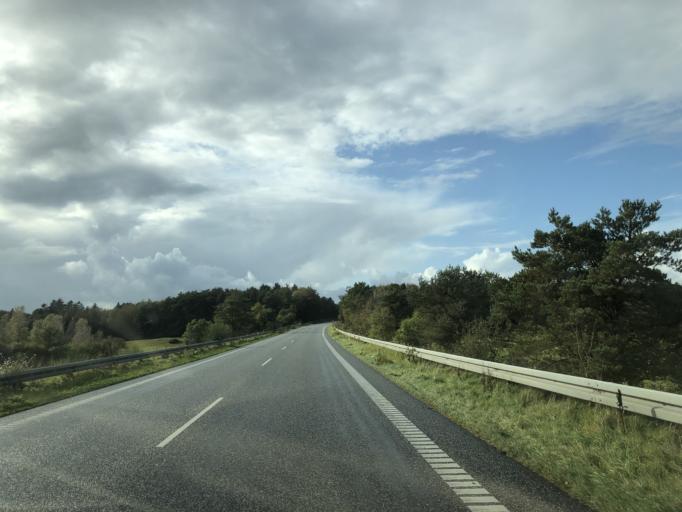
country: DK
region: North Denmark
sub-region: Vesthimmerland Kommune
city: Alestrup
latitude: 56.6111
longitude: 9.4295
